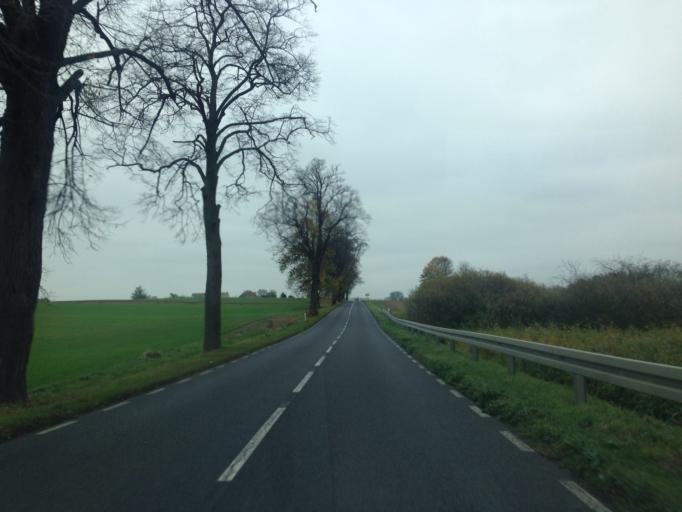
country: PL
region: Kujawsko-Pomorskie
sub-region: Powiat wabrzeski
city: Ksiazki
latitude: 53.3812
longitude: 19.0914
